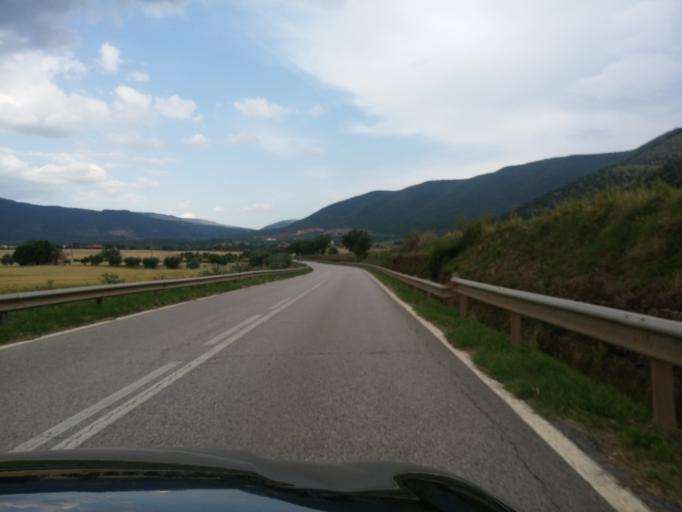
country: IT
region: Apulia
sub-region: Provincia di Foggia
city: Rignano Garganico
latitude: 41.7151
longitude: 15.5248
